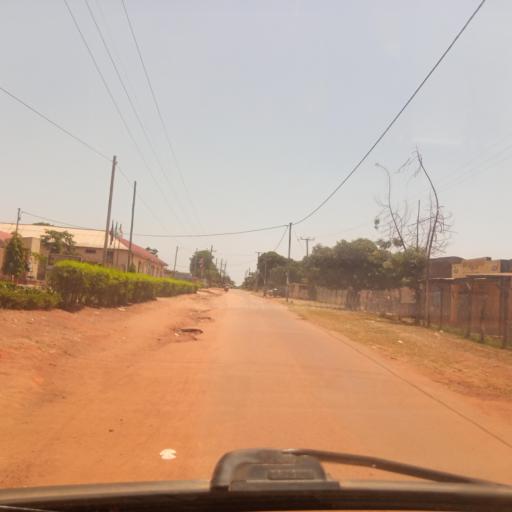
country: UG
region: Northern Region
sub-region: Lira District
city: Lira
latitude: 2.2533
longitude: 32.9009
